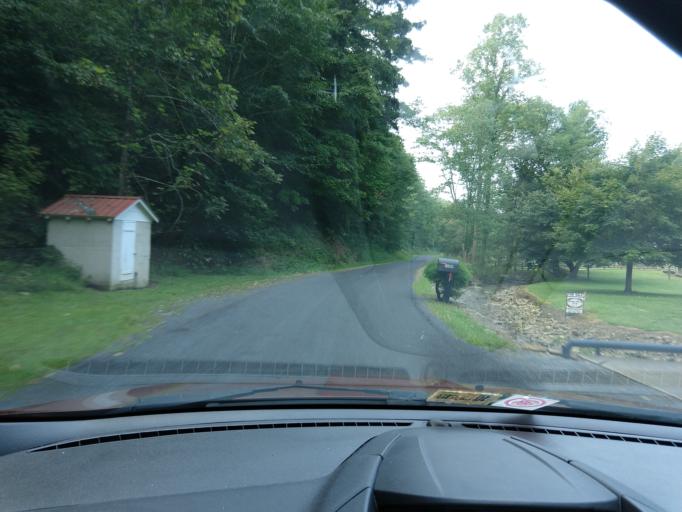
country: US
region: Virginia
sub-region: City of Covington
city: Covington
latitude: 37.9044
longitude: -80.0813
